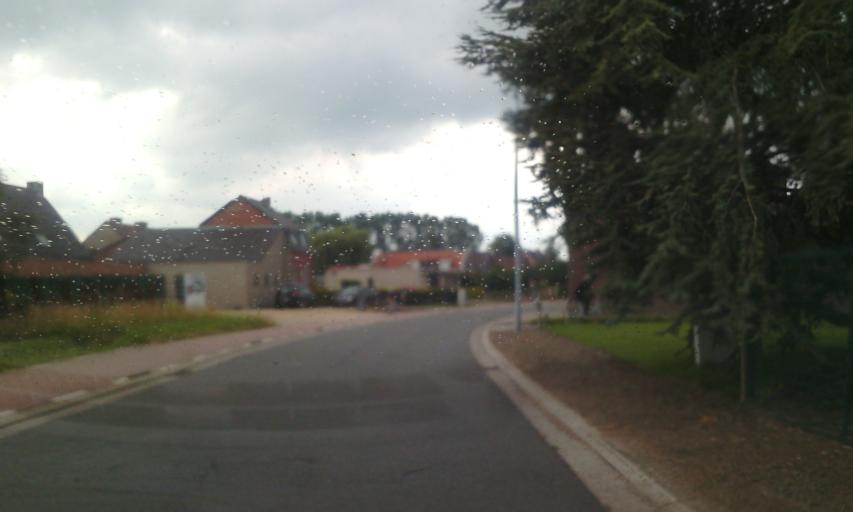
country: BE
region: Flanders
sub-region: Provincie Oost-Vlaanderen
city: Moerbeke
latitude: 51.1046
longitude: 3.9220
